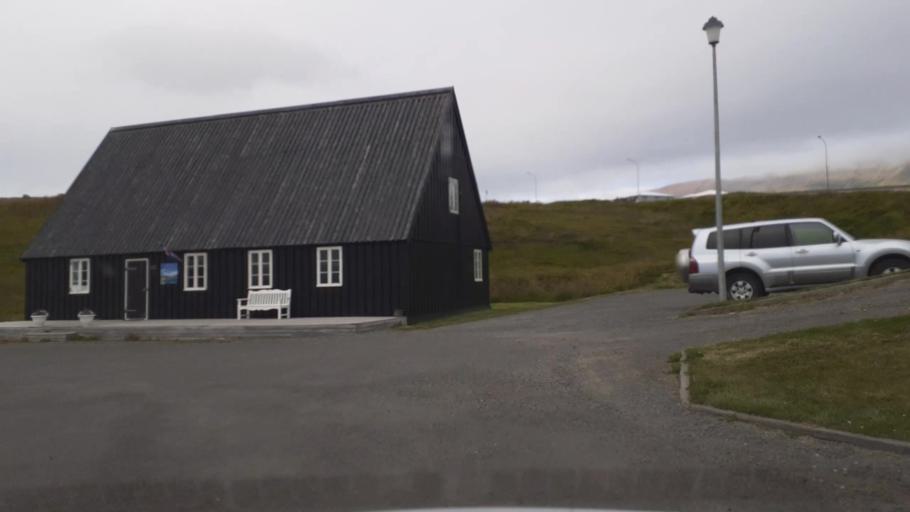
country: IS
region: Northwest
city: Saudarkrokur
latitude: 65.8989
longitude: -19.4167
